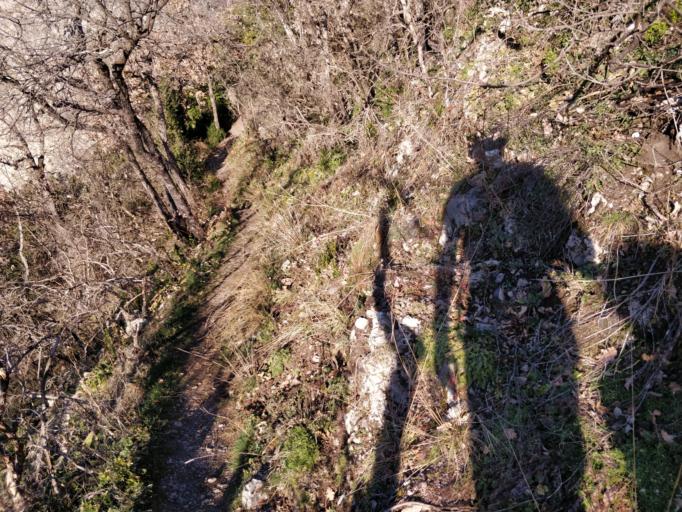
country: FR
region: Provence-Alpes-Cote d'Azur
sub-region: Departement des Alpes-de-Haute-Provence
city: Digne-les-Bains
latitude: 44.0942
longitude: 6.2487
